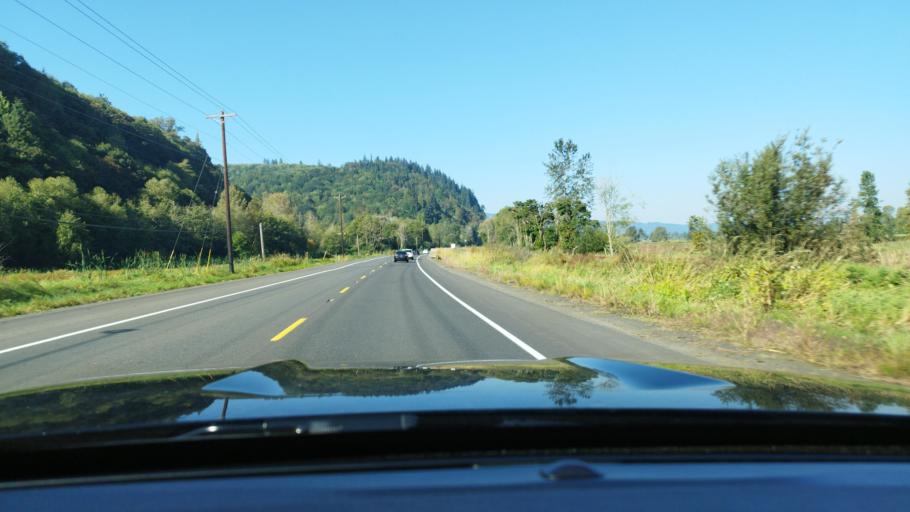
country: US
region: Oregon
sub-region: Columbia County
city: Clatskanie
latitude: 46.1107
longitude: -123.3024
